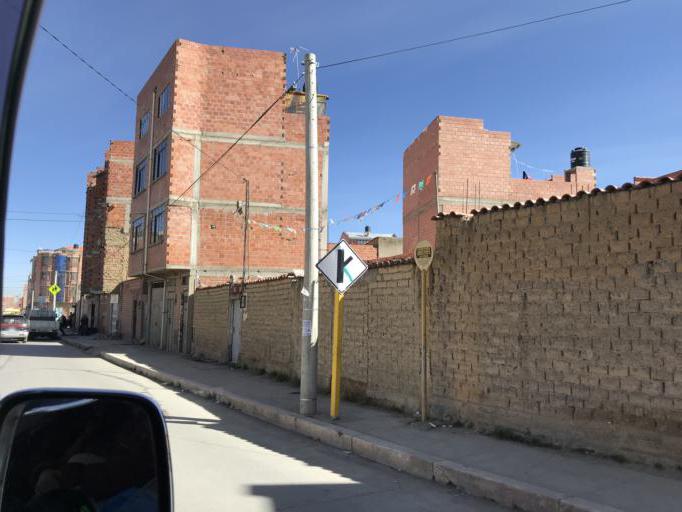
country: BO
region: La Paz
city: La Paz
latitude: -16.4869
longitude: -68.1888
